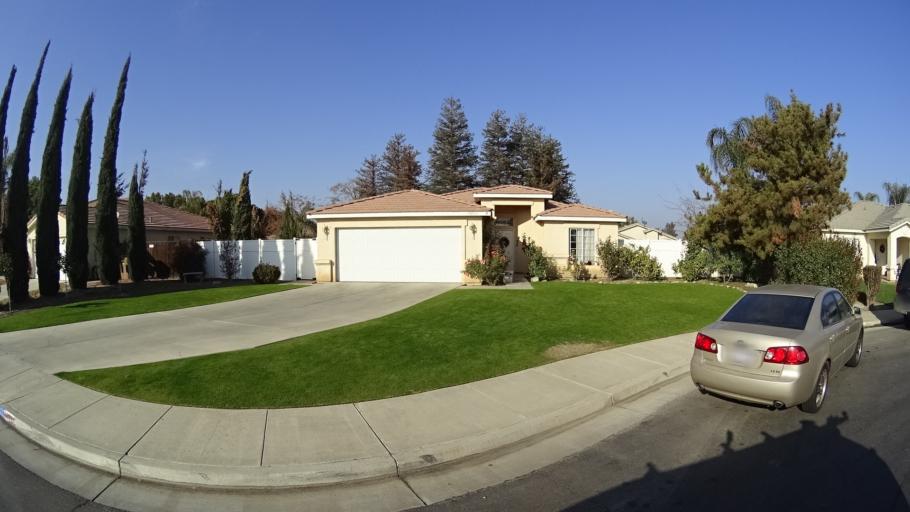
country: US
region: California
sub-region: Kern County
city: Rosedale
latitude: 35.3576
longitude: -119.1602
